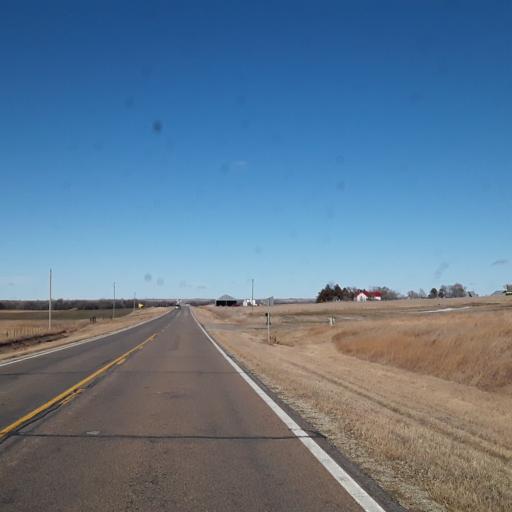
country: US
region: Kansas
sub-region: Lincoln County
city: Lincoln
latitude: 38.9626
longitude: -98.1512
